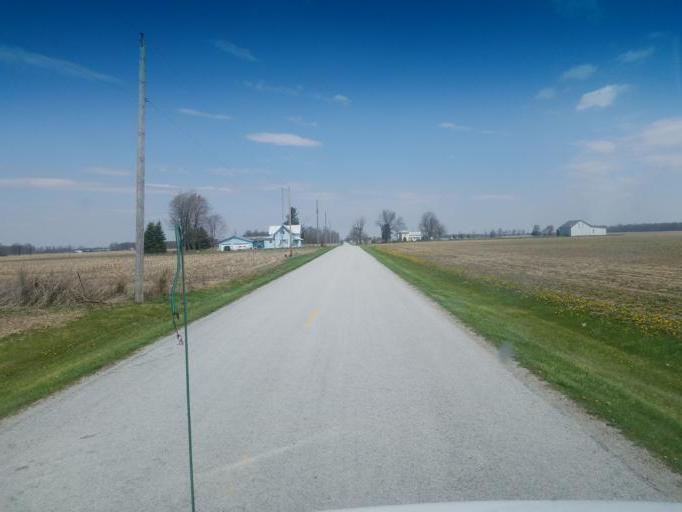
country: US
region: Ohio
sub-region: Hardin County
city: Forest
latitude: 40.7361
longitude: -83.5378
